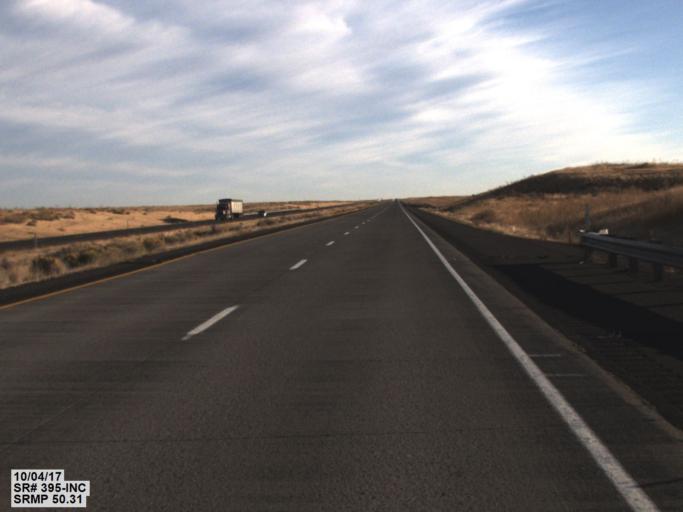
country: US
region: Washington
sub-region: Franklin County
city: Connell
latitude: 46.6057
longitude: -118.9210
